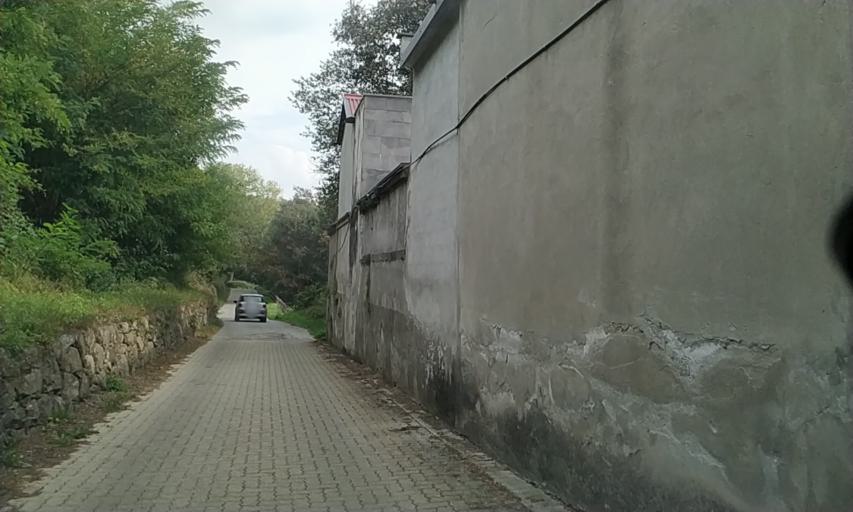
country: IT
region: Piedmont
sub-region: Provincia di Biella
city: Roppolo
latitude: 45.4215
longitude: 8.0796
